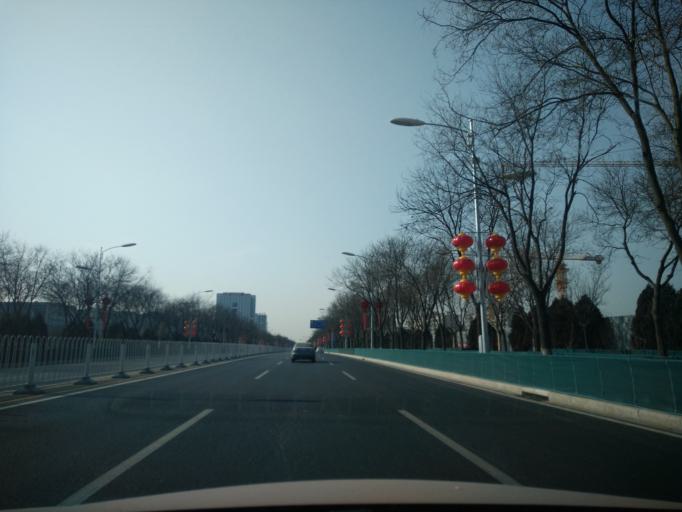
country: CN
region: Beijing
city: Jiugong
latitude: 39.7892
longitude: 116.4986
